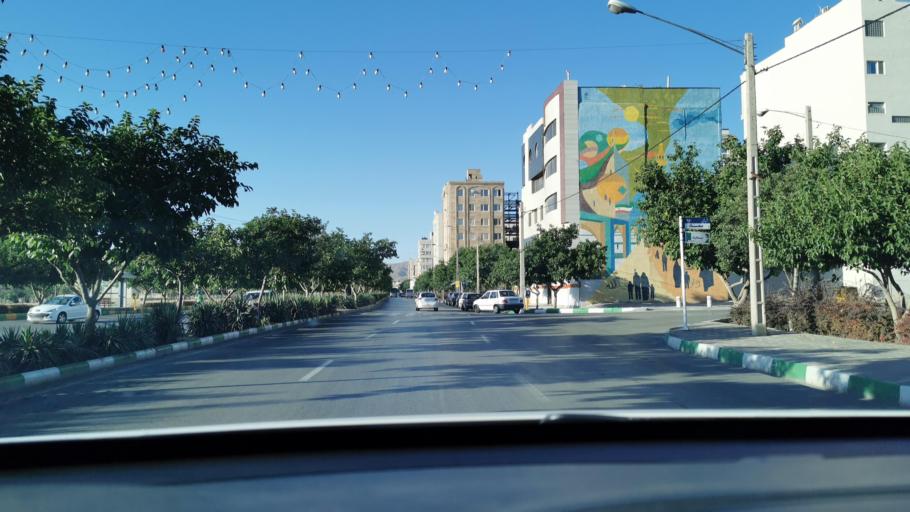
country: IR
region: Razavi Khorasan
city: Mashhad
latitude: 36.3548
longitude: 59.4880
